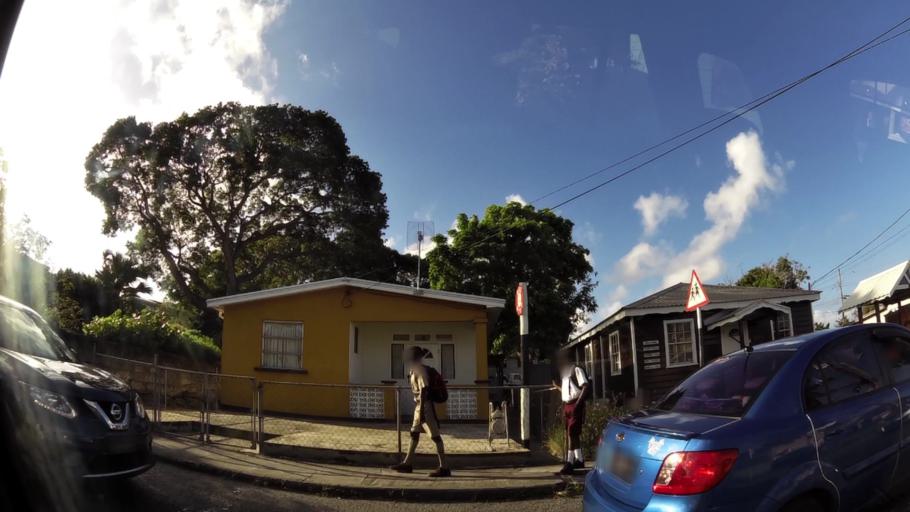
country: BB
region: Saint Michael
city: Bridgetown
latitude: 13.0931
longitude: -59.5920
